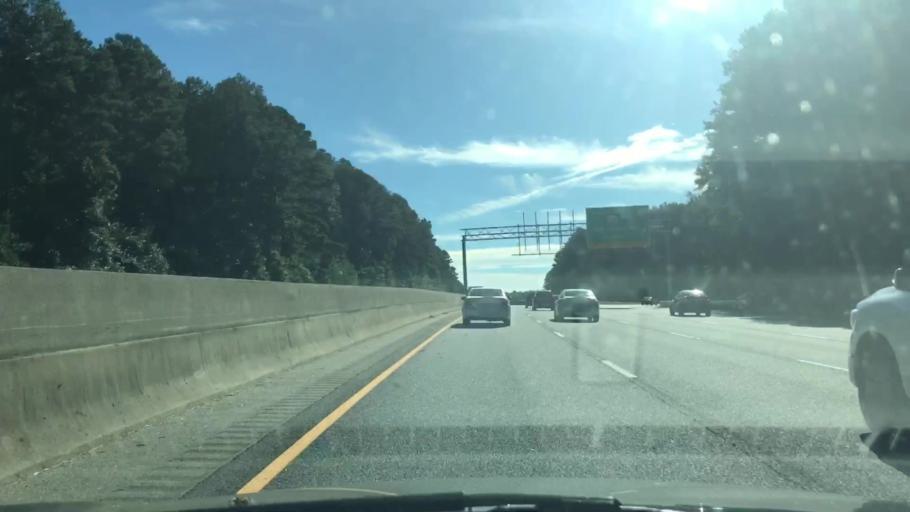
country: US
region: Georgia
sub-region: DeKalb County
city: Stone Mountain
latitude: 33.8241
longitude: -84.1495
